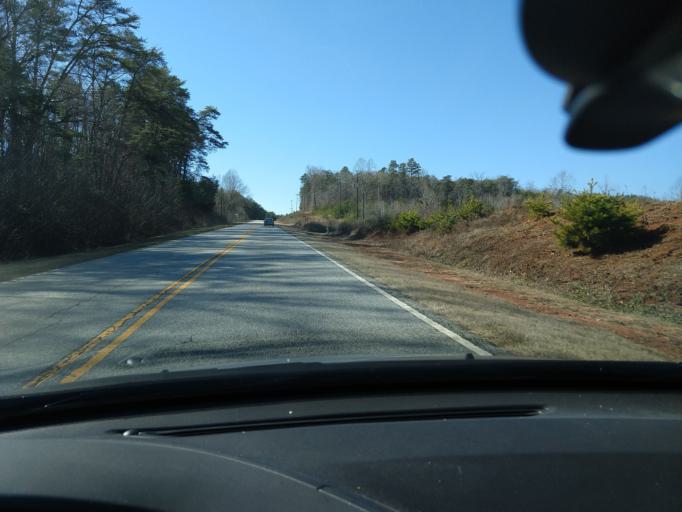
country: US
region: South Carolina
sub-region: Oconee County
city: Westminster
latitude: 34.6164
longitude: -83.1791
